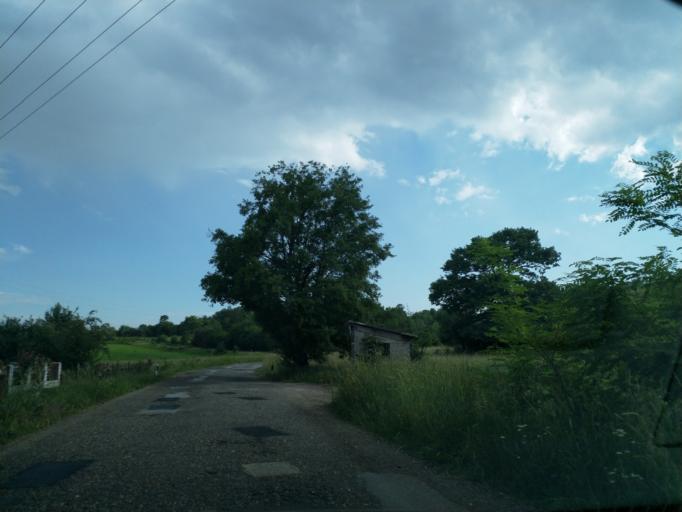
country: RS
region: Central Serbia
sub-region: Zajecarski Okrug
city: Boljevac
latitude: 43.9810
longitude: 21.9731
